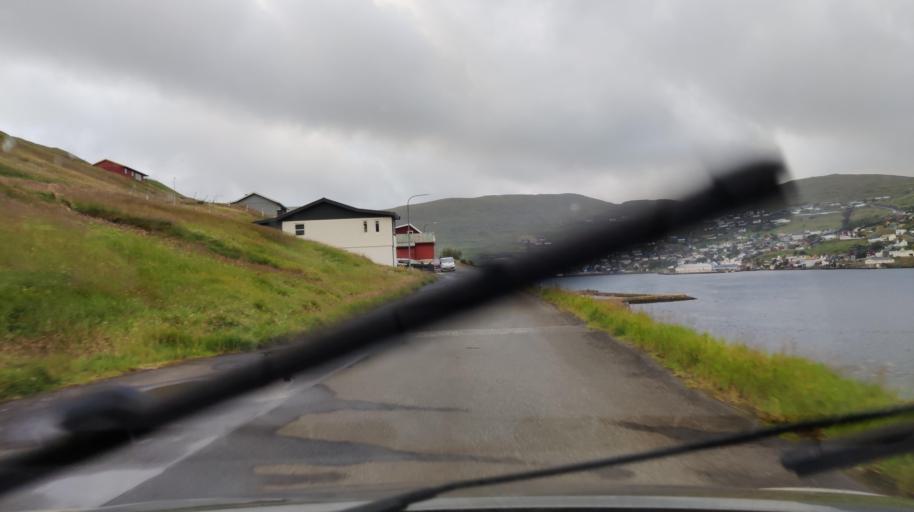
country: FO
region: Streymoy
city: Vestmanna
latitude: 62.1502
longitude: -7.1473
